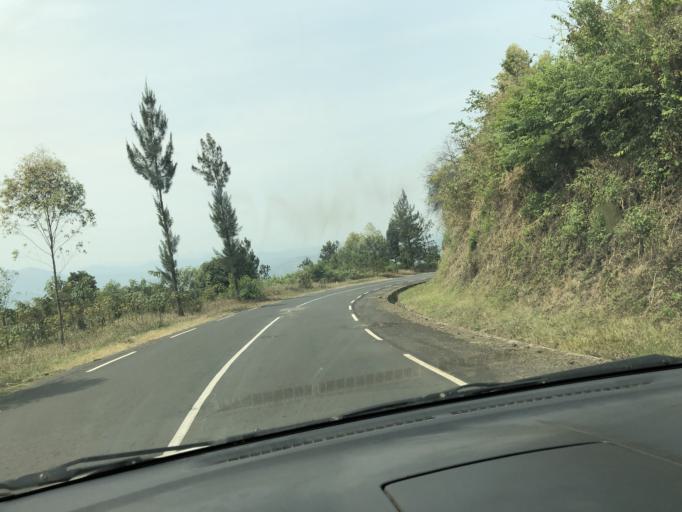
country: RW
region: Western Province
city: Cyangugu
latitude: -2.6673
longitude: 29.0011
